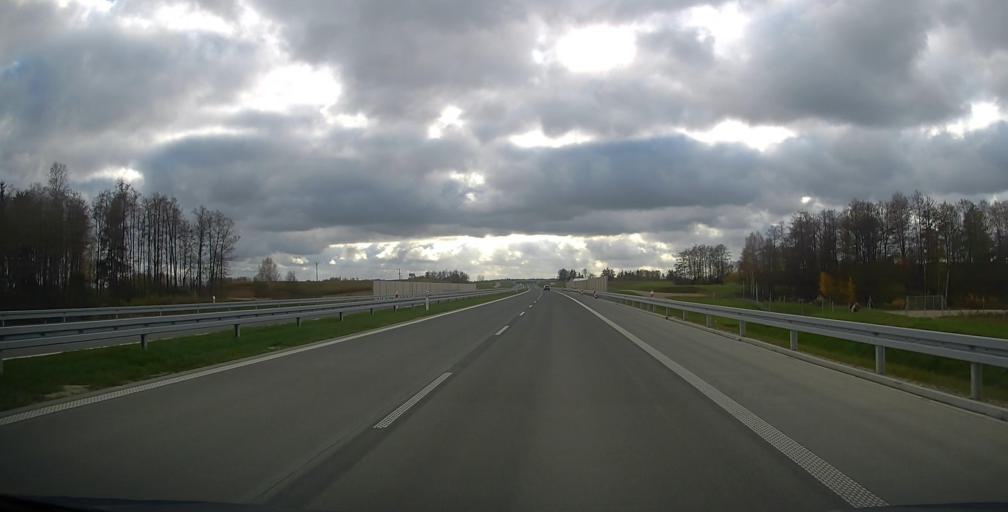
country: PL
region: Podlasie
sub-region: Powiat suwalski
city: Raczki
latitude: 53.9526
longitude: 22.7677
